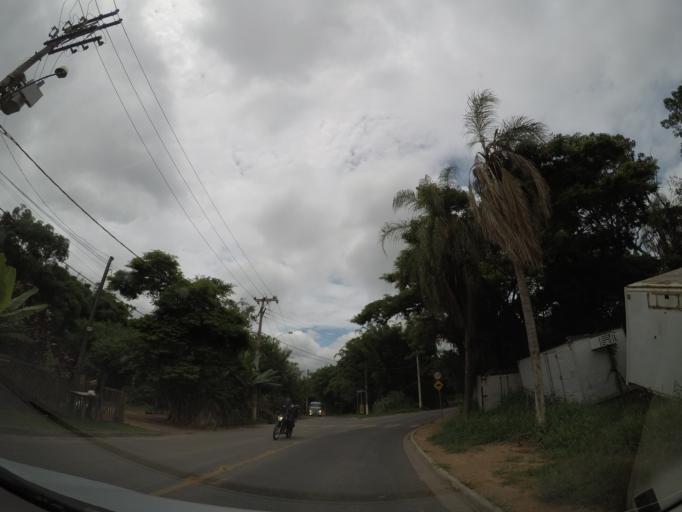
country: BR
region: Sao Paulo
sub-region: Louveira
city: Louveira
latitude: -23.0933
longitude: -46.9836
